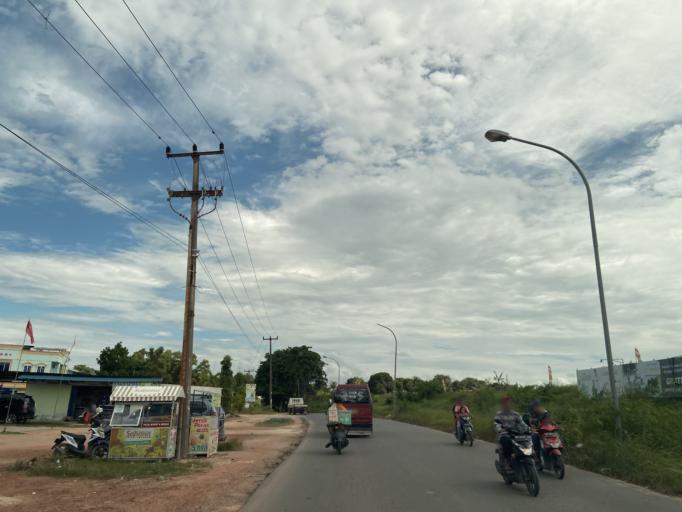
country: SG
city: Singapore
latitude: 1.0446
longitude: 103.9376
